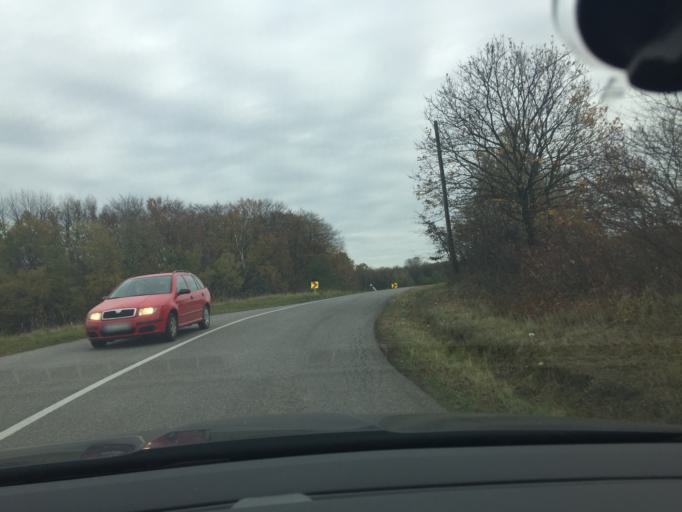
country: SK
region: Presovsky
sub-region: Okres Presov
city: Presov
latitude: 48.9458
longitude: 21.2976
